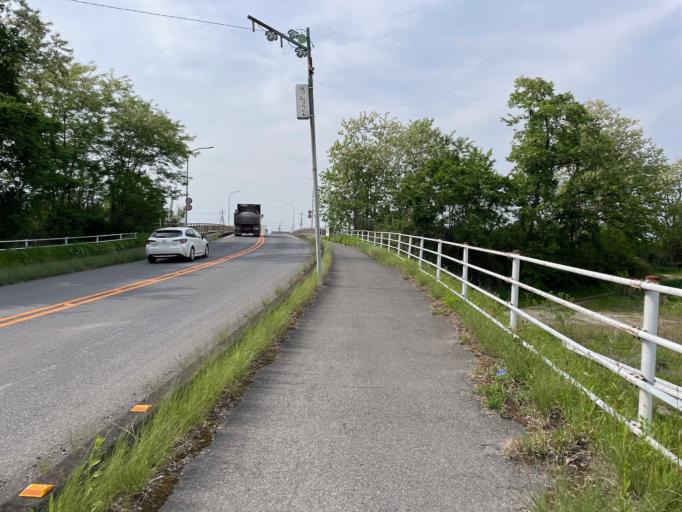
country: JP
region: Tochigi
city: Mibu
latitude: 36.4094
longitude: 139.8056
